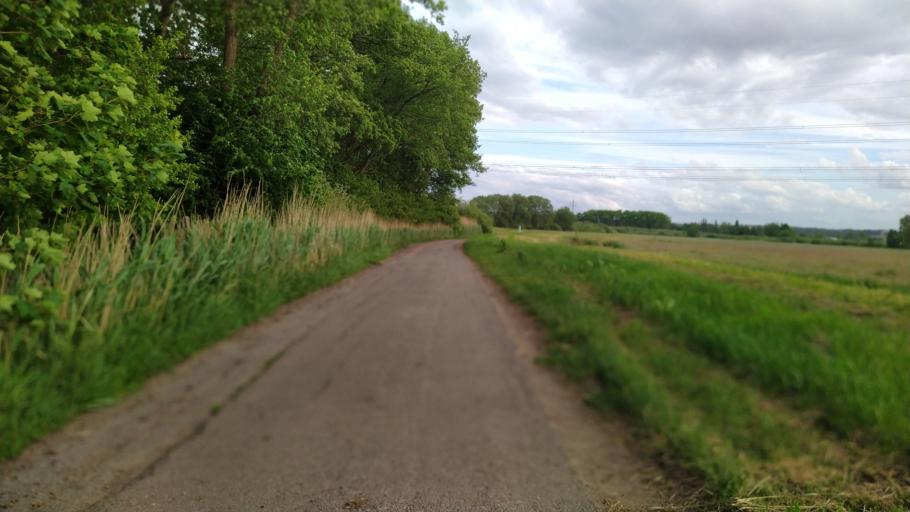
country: DE
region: Lower Saxony
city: Neu Wulmstorf
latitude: 53.4939
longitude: 9.8548
